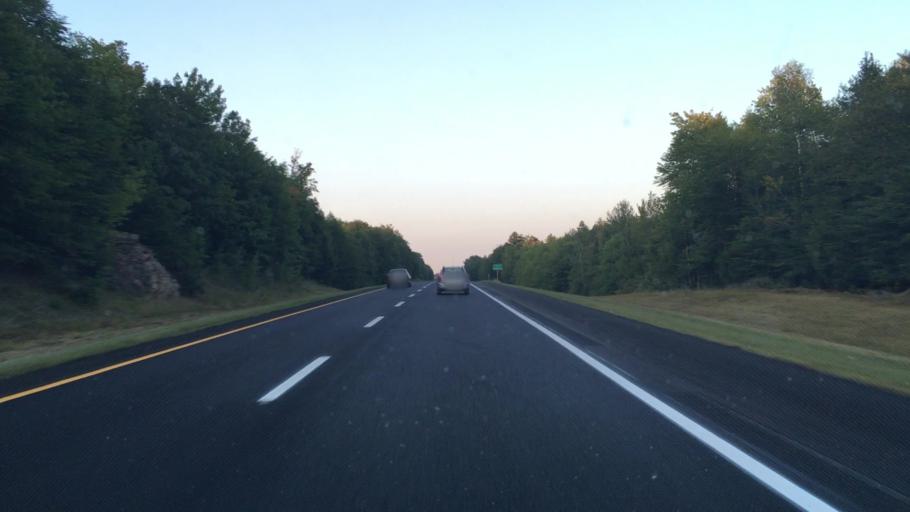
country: US
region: Maine
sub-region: Sagadahoc County
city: Topsham
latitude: 43.9955
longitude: -69.9353
